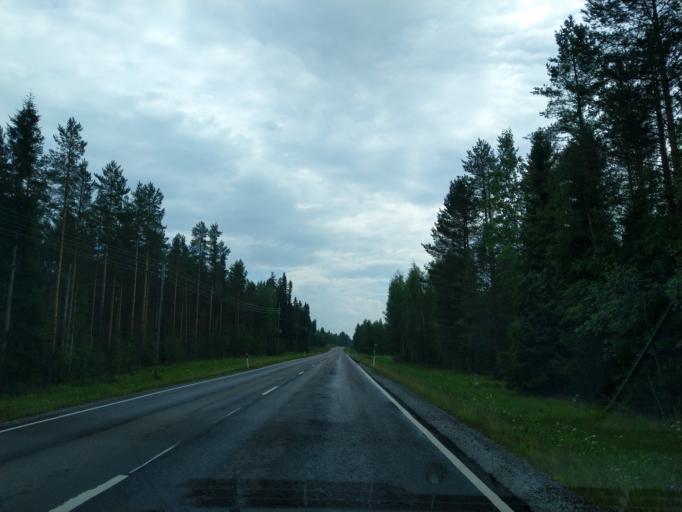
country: FI
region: Southern Savonia
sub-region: Savonlinna
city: Punkaharju
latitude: 61.6449
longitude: 29.4248
